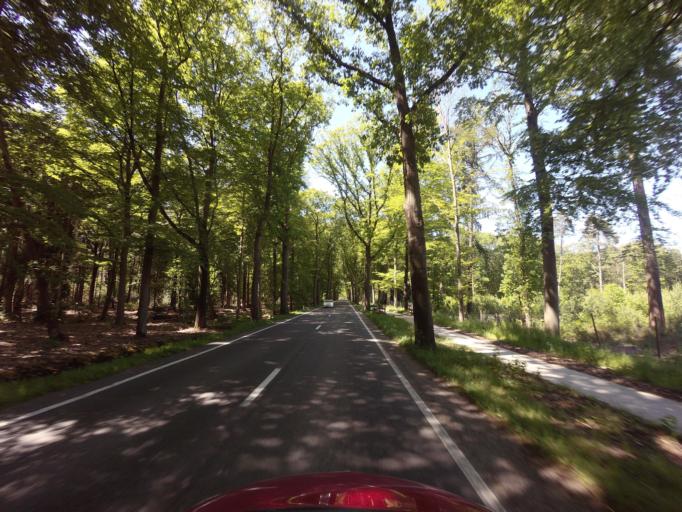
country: BE
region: Flanders
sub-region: Provincie Antwerpen
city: Ravels
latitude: 51.3747
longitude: 5.0416
